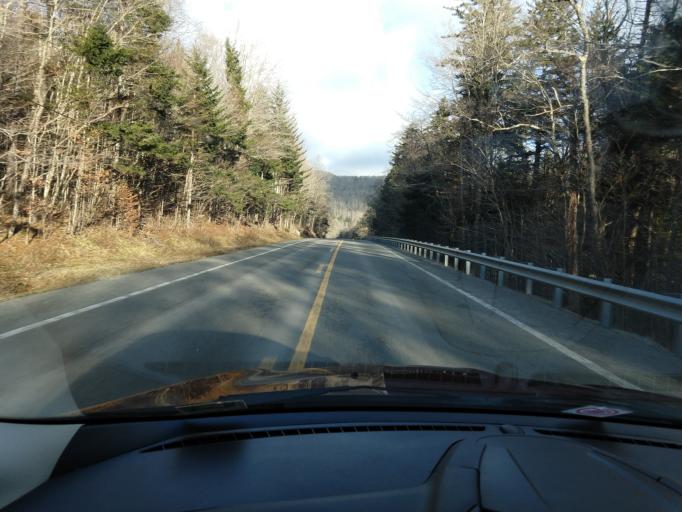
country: US
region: West Virginia
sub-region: Randolph County
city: Elkins
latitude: 38.6108
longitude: -79.8664
